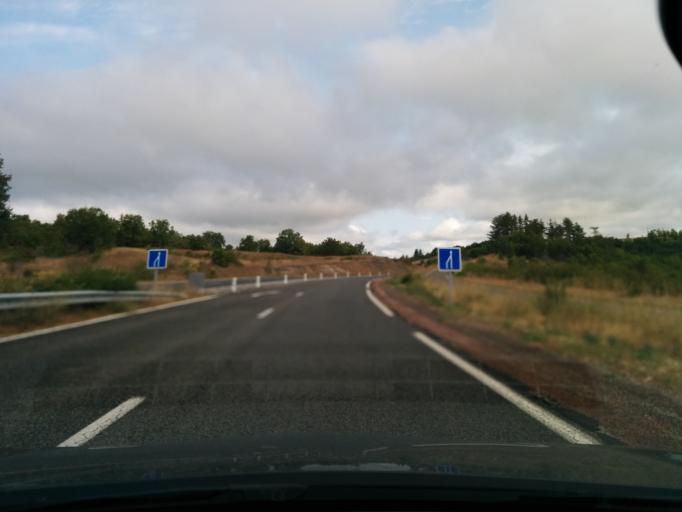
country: FR
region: Midi-Pyrenees
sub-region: Departement du Lot
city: Pradines
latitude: 44.5116
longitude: 1.4441
